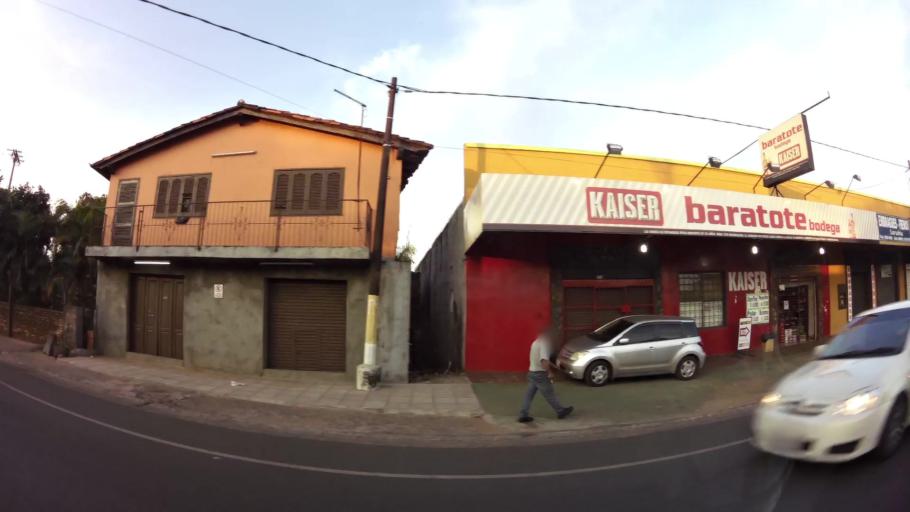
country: PY
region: Central
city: San Lorenzo
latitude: -25.3476
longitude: -57.4971
